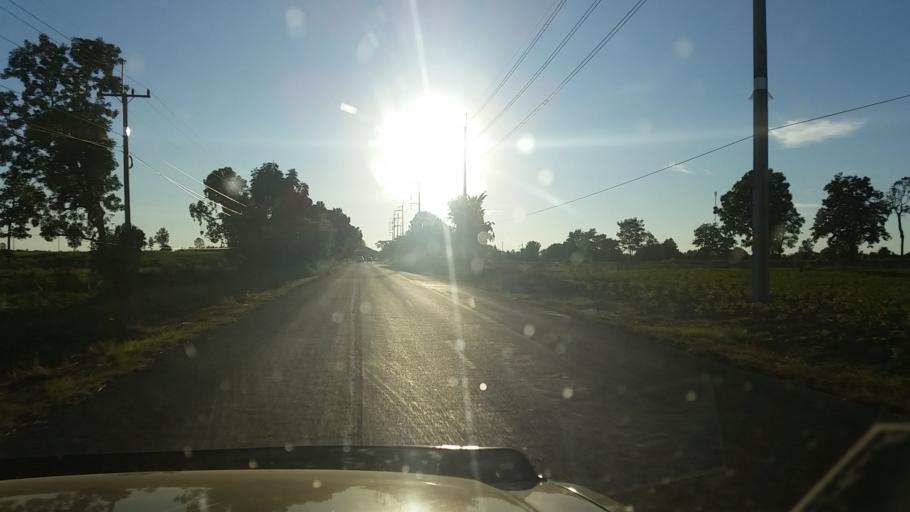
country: TH
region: Chaiyaphum
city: Sap Yai
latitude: 15.6602
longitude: 101.6593
